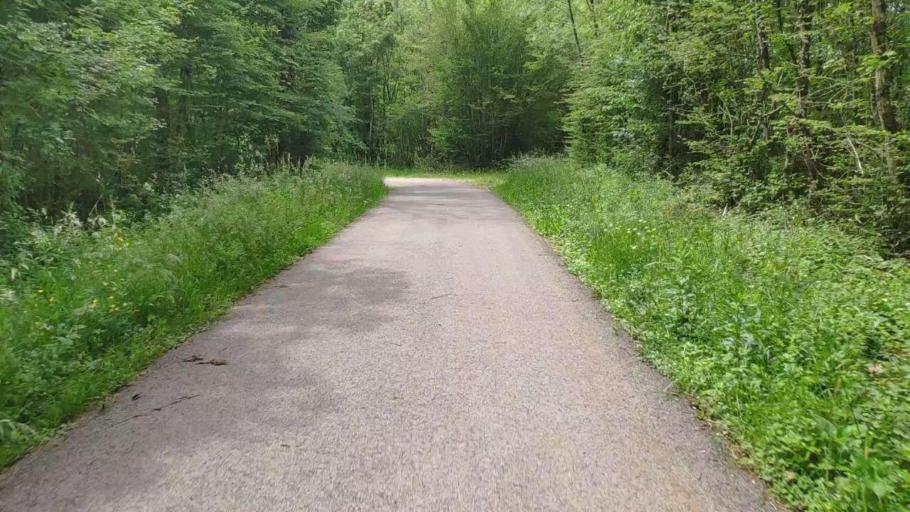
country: FR
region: Franche-Comte
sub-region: Departement du Jura
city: Perrigny
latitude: 46.7456
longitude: 5.6405
